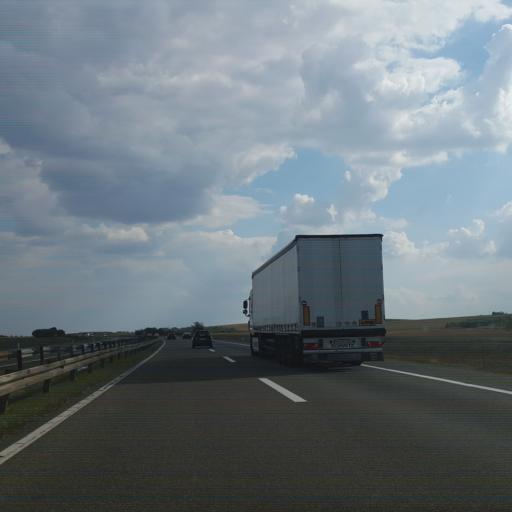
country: RS
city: Lugavcina
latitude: 44.5135
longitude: 21.0139
